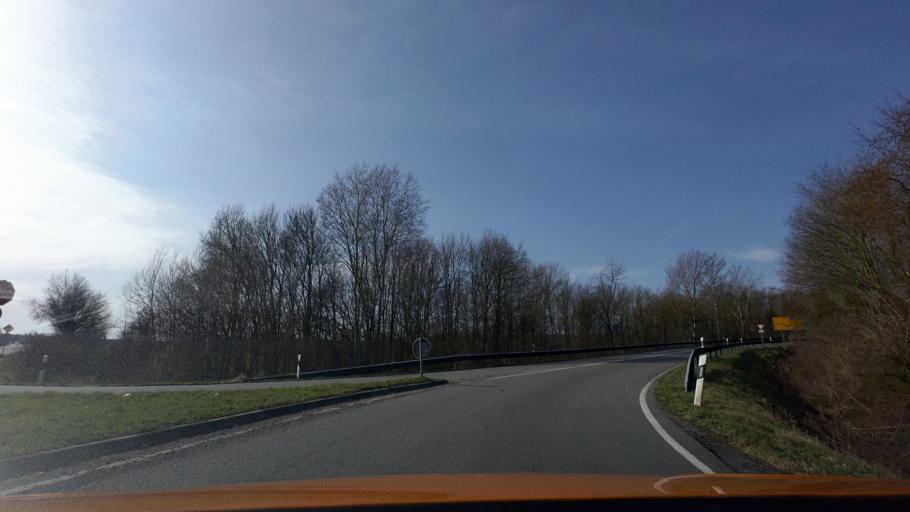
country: DE
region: North Rhine-Westphalia
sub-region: Regierungsbezirk Detmold
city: Petershagen
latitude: 52.3794
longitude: 8.9538
